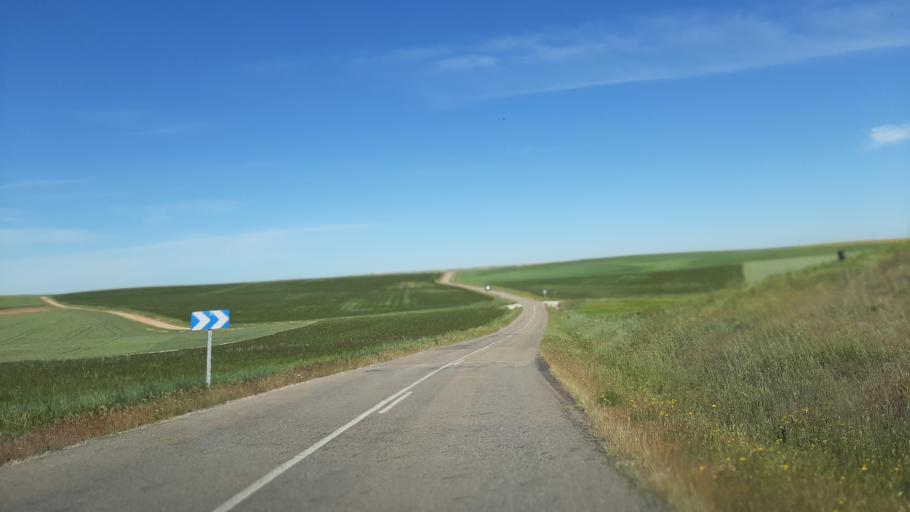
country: ES
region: Castille and Leon
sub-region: Provincia de Salamanca
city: Pedrosillo de Alba
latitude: 40.8231
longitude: -5.4193
